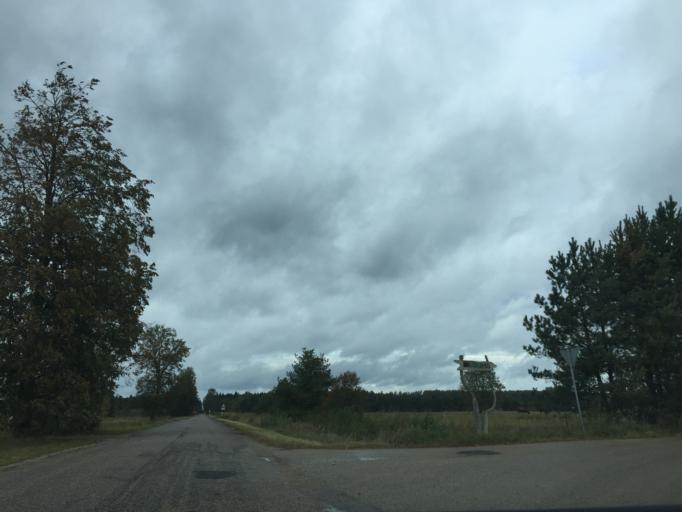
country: LV
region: Olaine
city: Olaine
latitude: 56.7679
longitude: 23.8782
